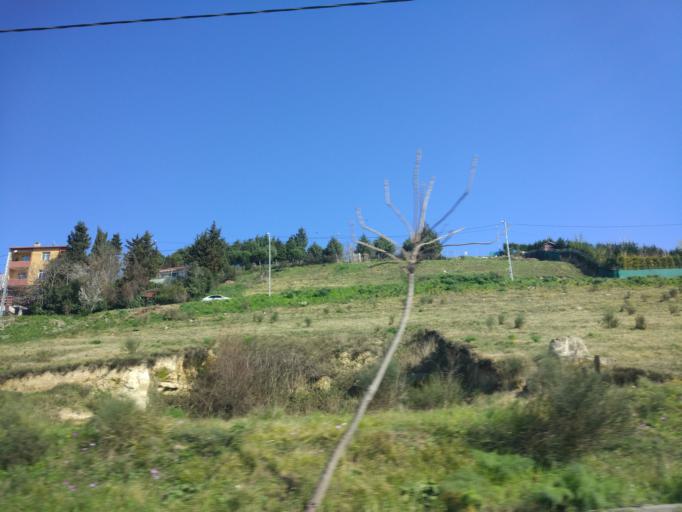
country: TR
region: Istanbul
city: Basaksehir
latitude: 41.0493
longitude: 28.7489
